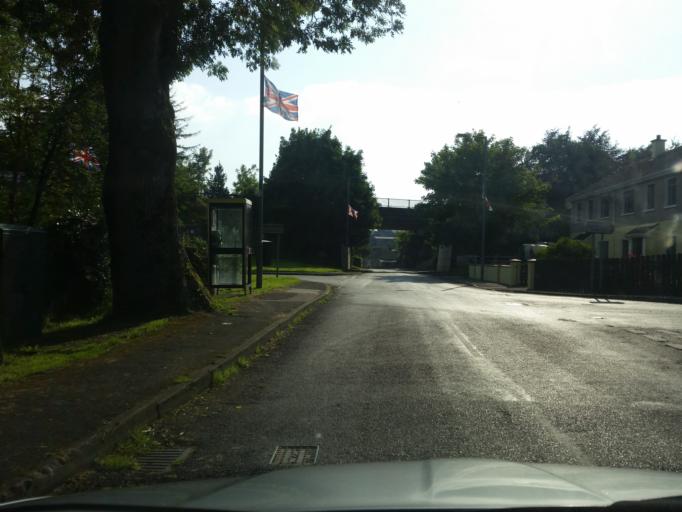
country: GB
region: Northern Ireland
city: Ballinamallard
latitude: 54.3190
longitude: -7.5336
